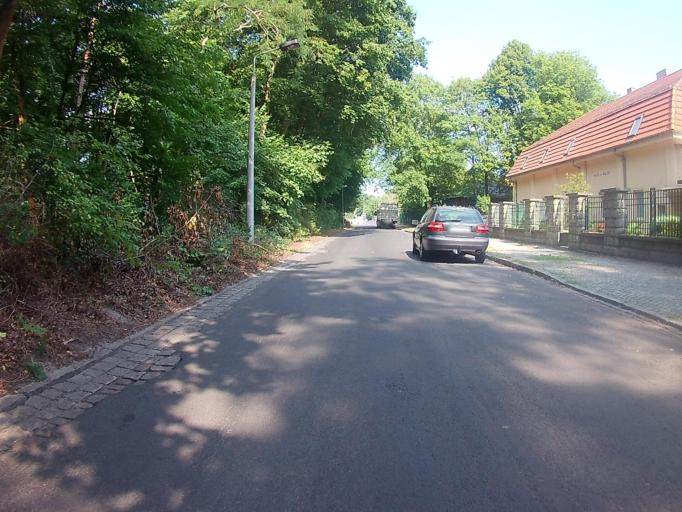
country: DE
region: Berlin
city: Grunau
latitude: 52.4102
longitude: 13.5914
